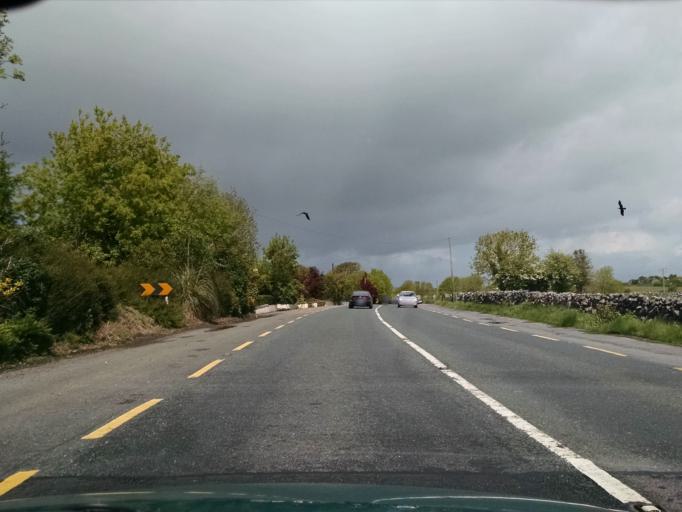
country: IE
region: Connaught
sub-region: County Galway
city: Oranmore
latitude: 53.2471
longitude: -8.8998
